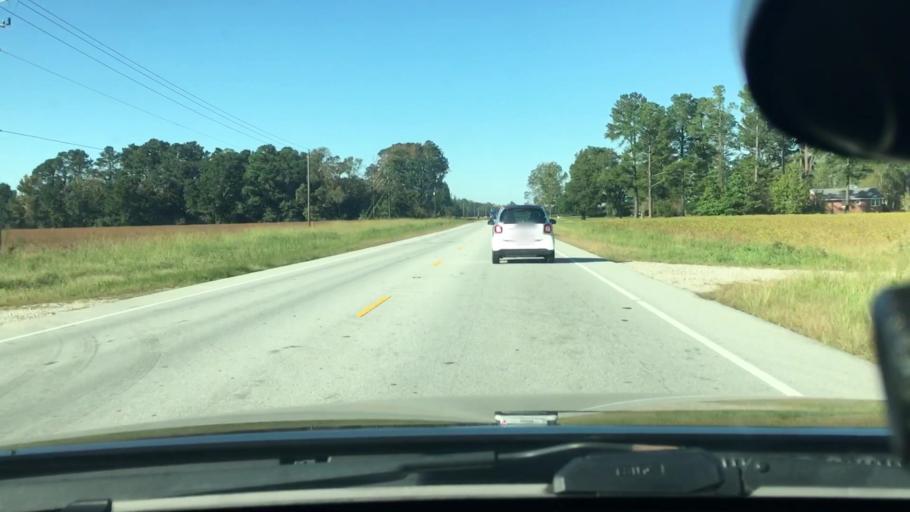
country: US
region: North Carolina
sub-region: Craven County
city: Trent Woods
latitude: 35.1855
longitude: -77.1316
